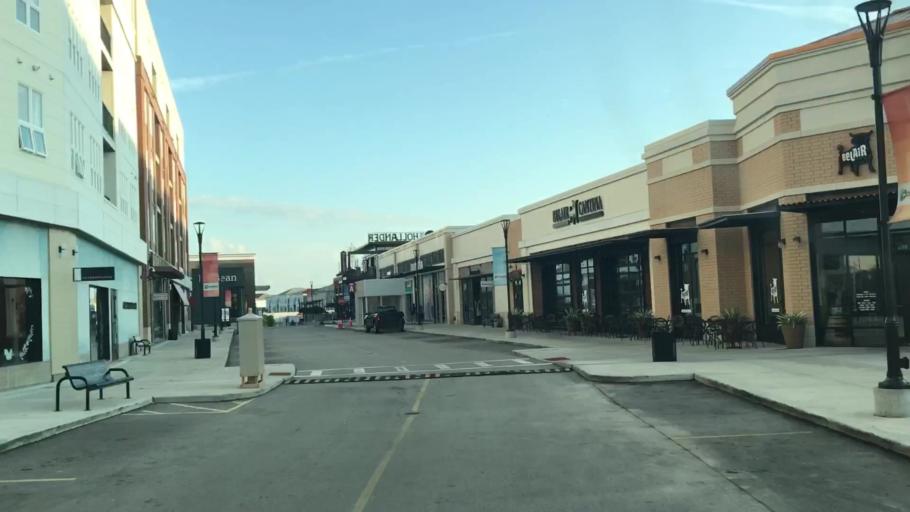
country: US
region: Wisconsin
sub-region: Waukesha County
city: Brookfield
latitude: 43.0343
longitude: -88.1638
